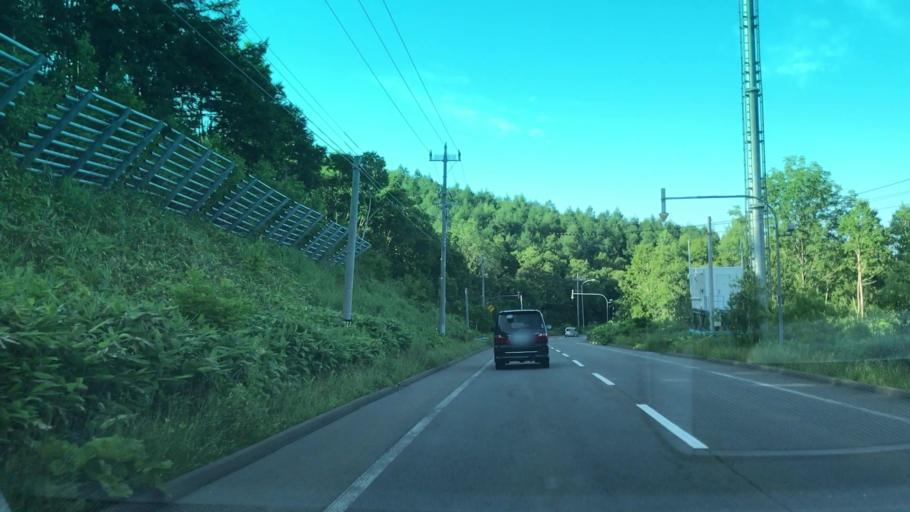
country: JP
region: Hokkaido
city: Otaru
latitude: 43.1080
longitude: 141.0049
